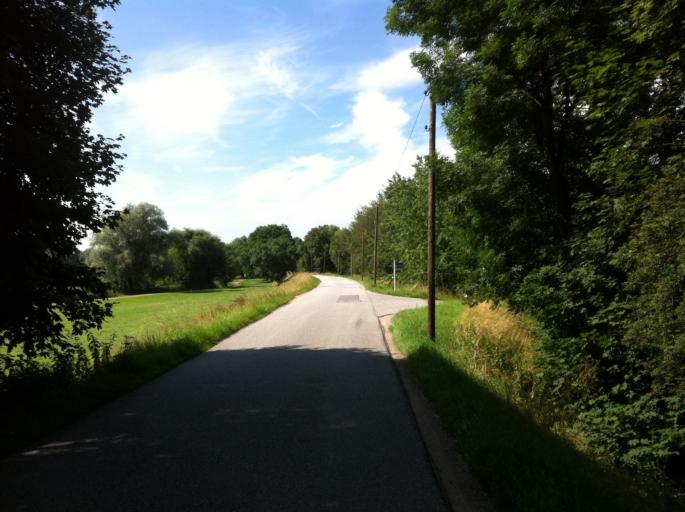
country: DE
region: Hamburg
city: Rothenburgsort
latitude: 53.4878
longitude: 10.0853
